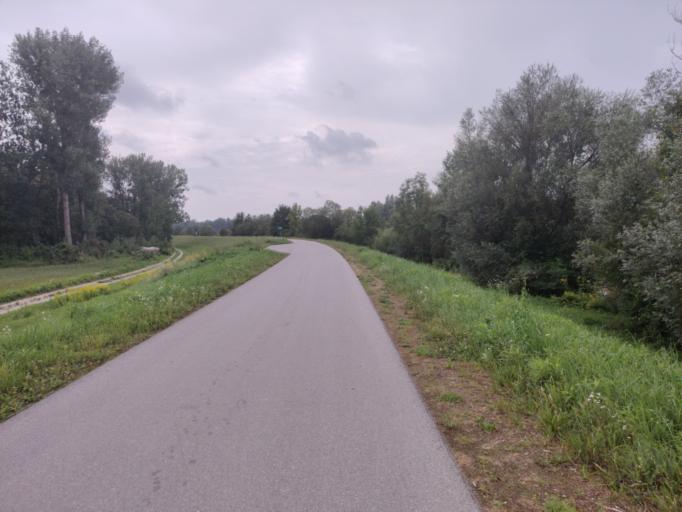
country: AT
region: Lower Austria
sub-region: Politischer Bezirk Amstetten
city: Ennsdorf
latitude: 48.2339
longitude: 14.5649
